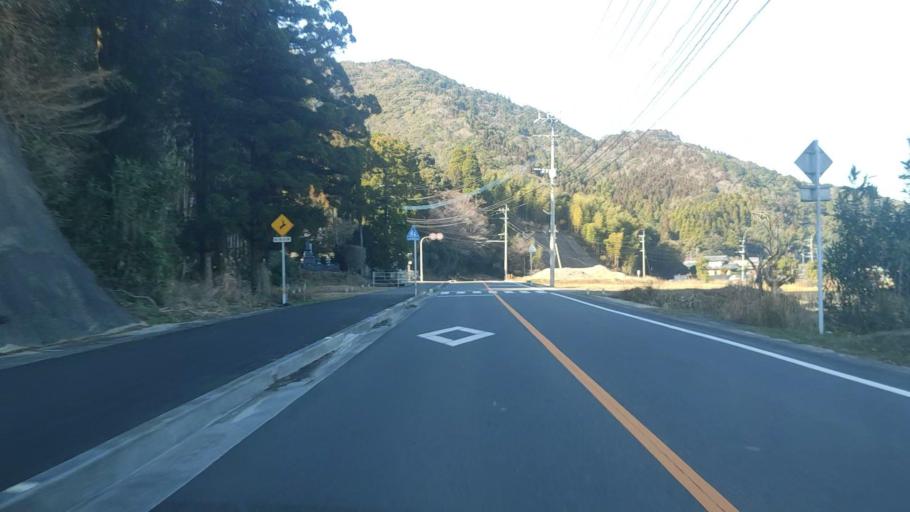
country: JP
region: Oita
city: Saiki
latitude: 32.9251
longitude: 131.9252
